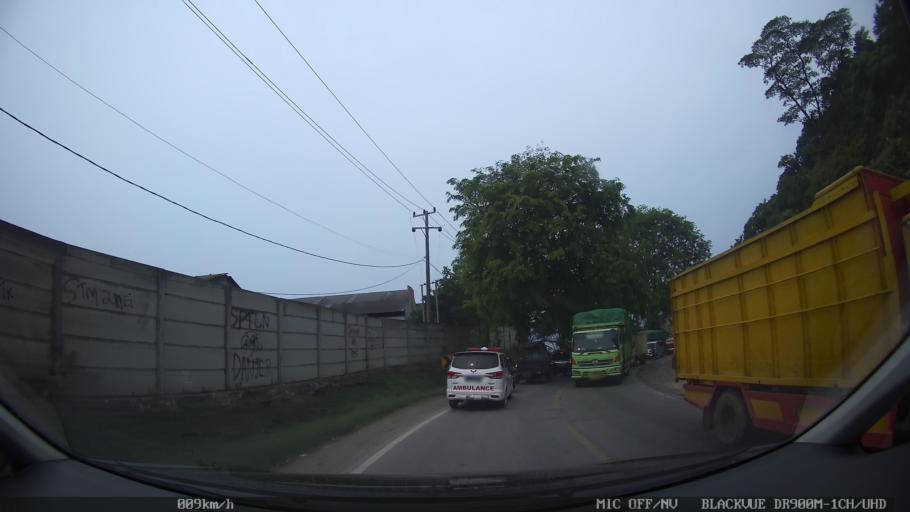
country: ID
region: Lampung
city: Panjang
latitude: -5.4414
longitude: 105.3159
